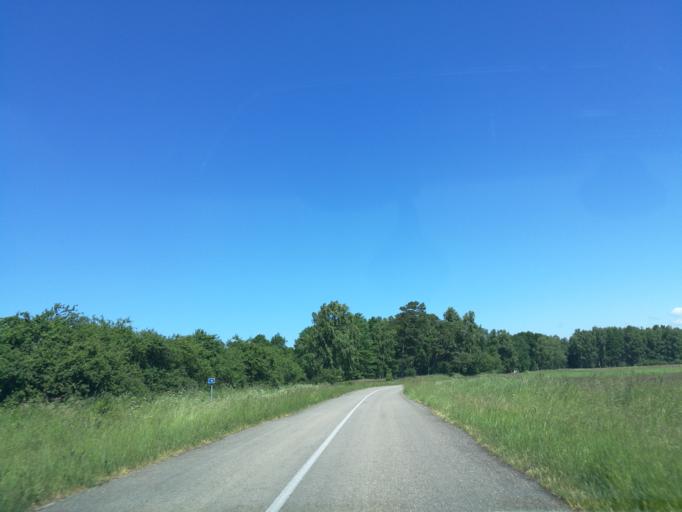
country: LT
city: Neringa
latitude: 55.3763
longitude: 21.2238
